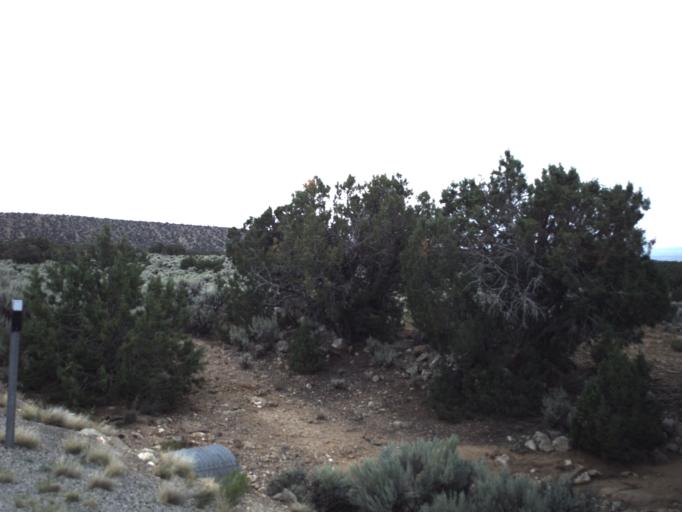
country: US
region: Utah
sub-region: Carbon County
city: East Carbon City
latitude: 39.4616
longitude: -110.3909
